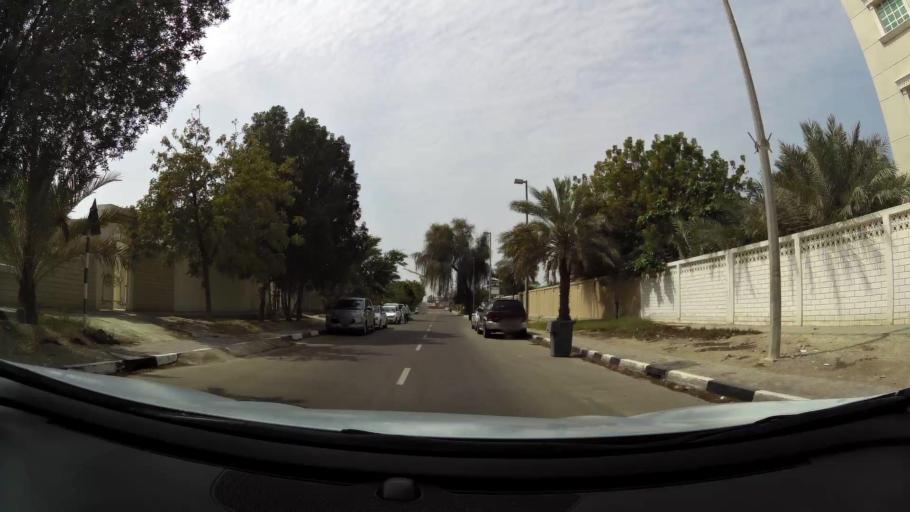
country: AE
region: Abu Dhabi
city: Abu Dhabi
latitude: 24.5356
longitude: 54.6887
